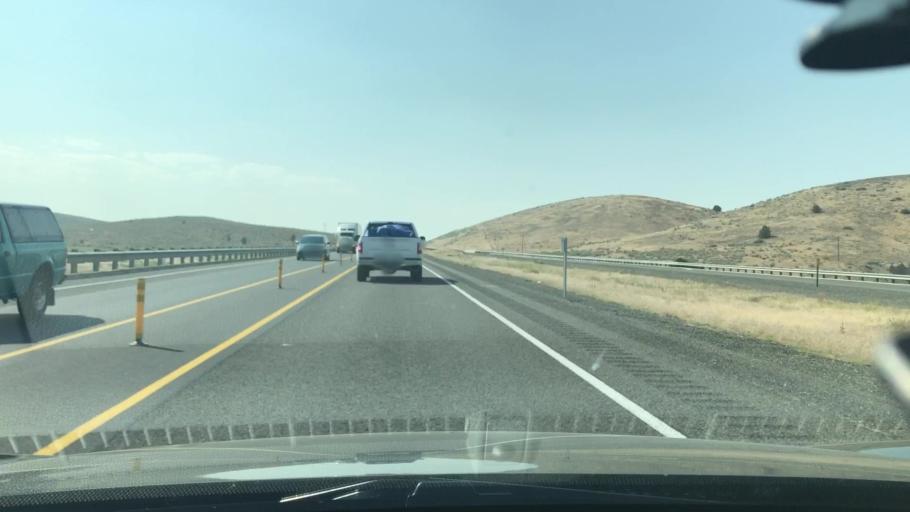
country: US
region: Oregon
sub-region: Baker County
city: Baker City
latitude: 44.6811
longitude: -117.6550
